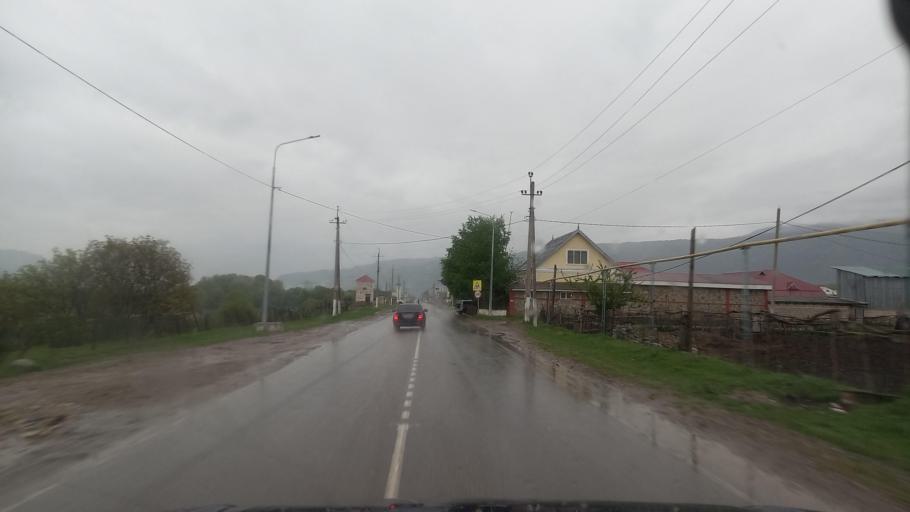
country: RU
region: Kabardino-Balkariya
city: Zhankhoteko
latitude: 43.5893
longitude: 43.2023
